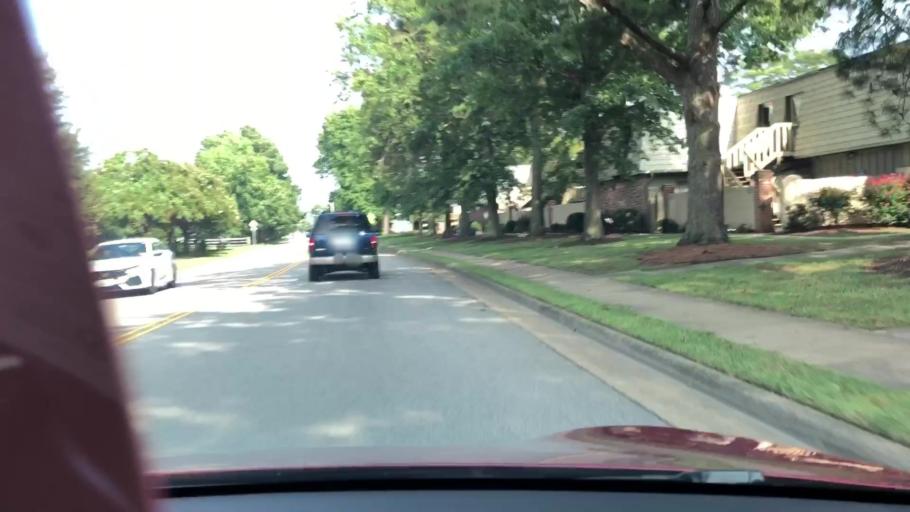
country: US
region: Virginia
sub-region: City of Virginia Beach
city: Virginia Beach
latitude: 36.8378
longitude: -75.9927
